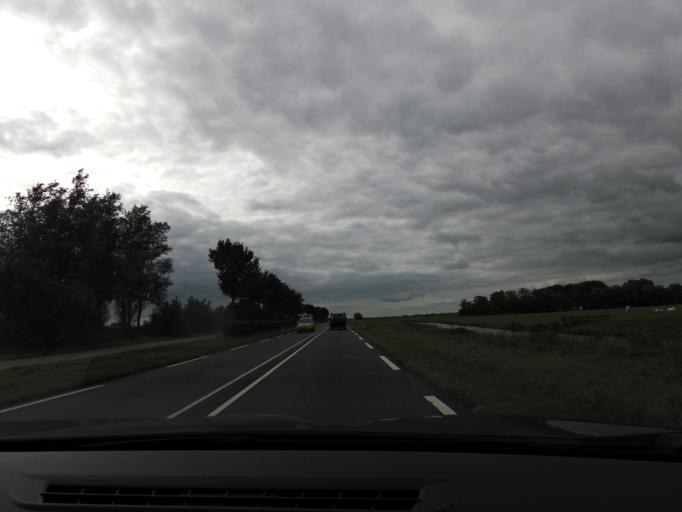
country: NL
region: Utrecht
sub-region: Gemeente Lopik
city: Lopik
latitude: 51.9985
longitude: 4.9892
